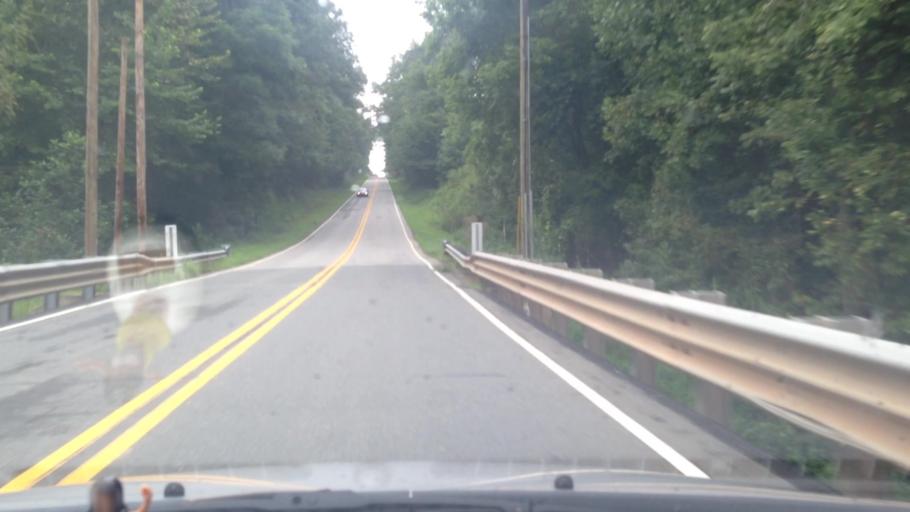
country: US
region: North Carolina
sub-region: Stokes County
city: Danbury
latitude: 36.4014
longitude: -80.1382
